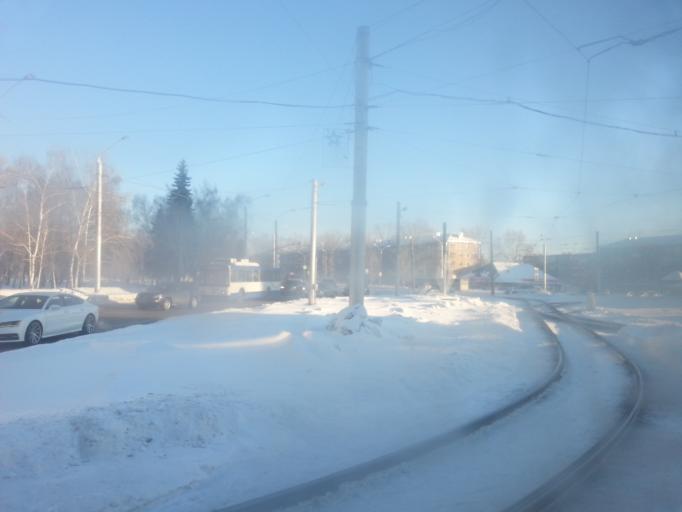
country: RU
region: Altai Krai
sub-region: Gorod Barnaulskiy
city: Barnaul
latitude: 53.3598
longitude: 83.7000
